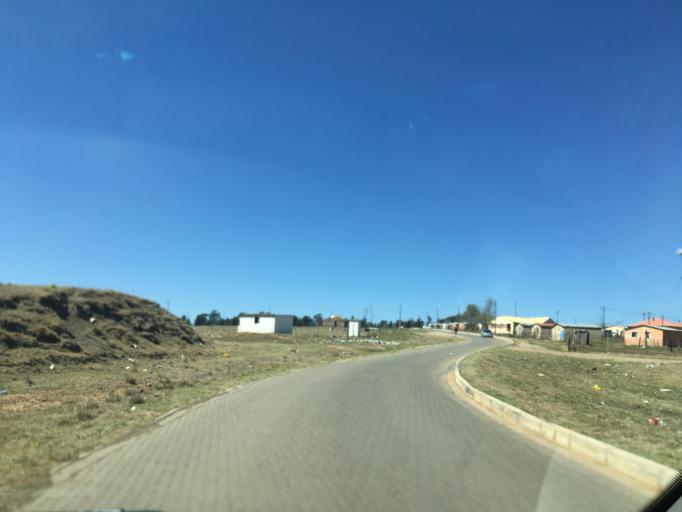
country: ZA
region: Eastern Cape
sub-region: Chris Hani District Municipality
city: Elliot
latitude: -31.3319
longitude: 27.8327
